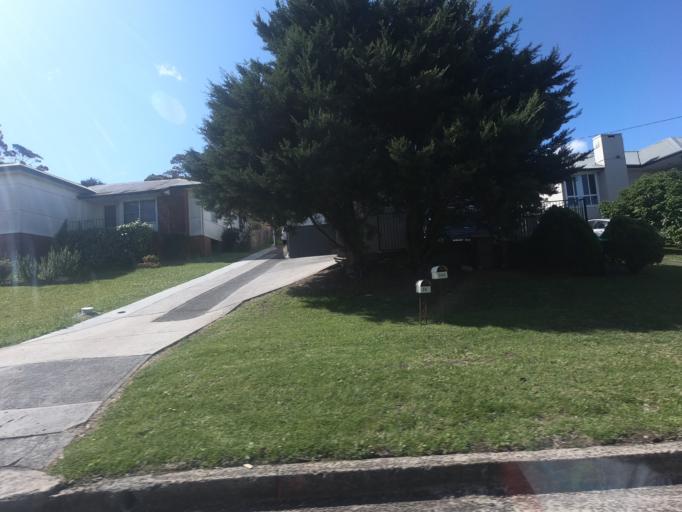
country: AU
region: New South Wales
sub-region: Wollongong
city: Cordeaux Heights
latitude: -34.4508
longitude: 150.8409
